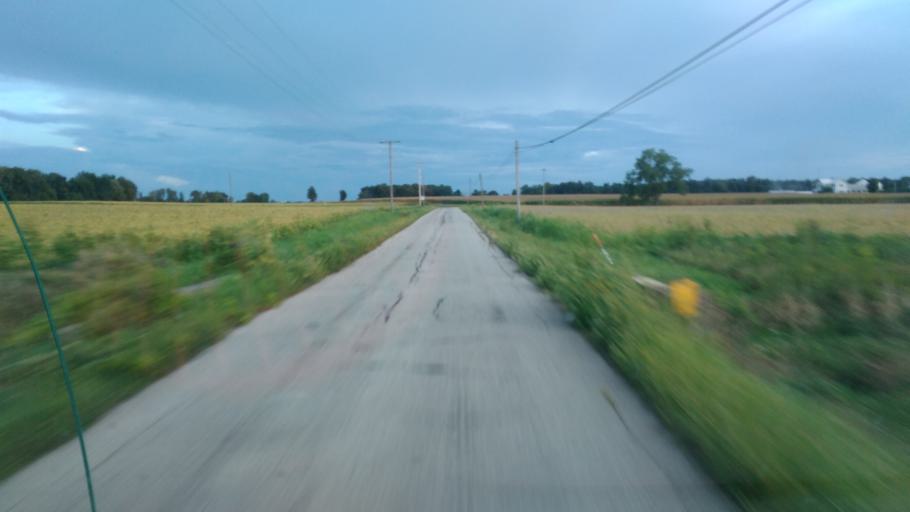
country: US
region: Ohio
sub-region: Crawford County
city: Bucyrus
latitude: 40.7061
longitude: -82.9190
